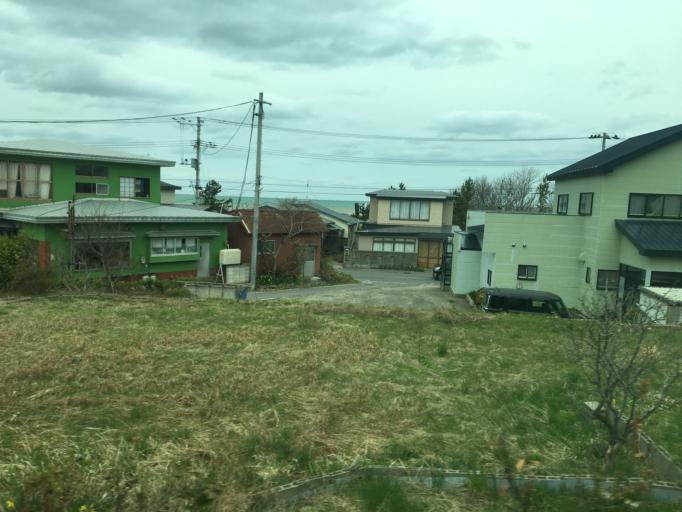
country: JP
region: Aomori
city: Shimokizukuri
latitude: 40.7801
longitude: 140.2260
